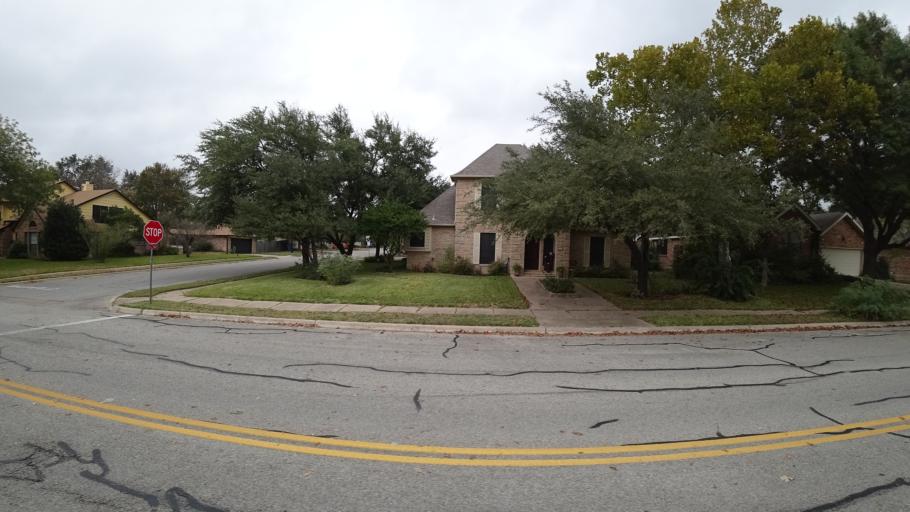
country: US
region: Texas
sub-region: Travis County
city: Pflugerville
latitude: 30.4447
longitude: -97.6144
